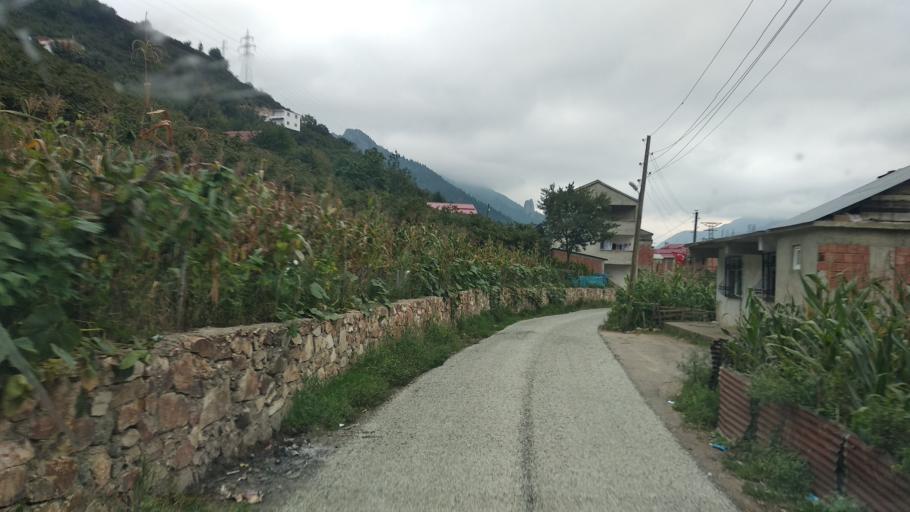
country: TR
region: Giresun
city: Dogankent
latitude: 40.7472
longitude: 38.9869
